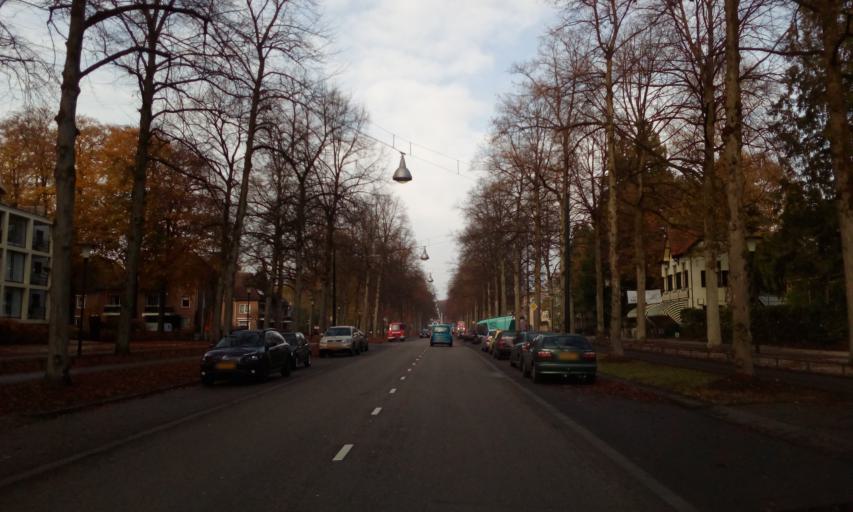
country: NL
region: Gelderland
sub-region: Gemeente Apeldoorn
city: Apeldoorn
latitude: 52.2236
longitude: 5.9515
